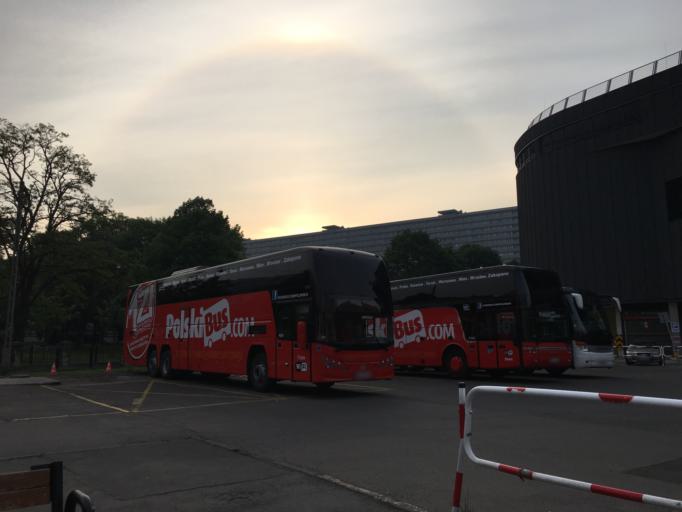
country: PL
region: Silesian Voivodeship
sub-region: Katowice
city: Katowice
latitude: 50.2625
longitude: 19.0176
